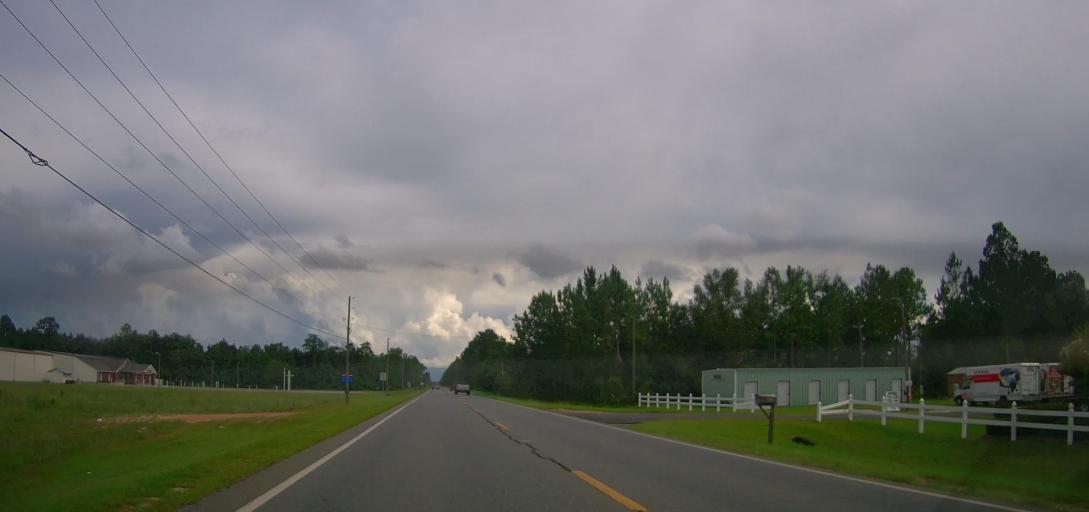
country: US
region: Georgia
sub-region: Wayne County
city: Jesup
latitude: 31.6435
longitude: -81.9067
